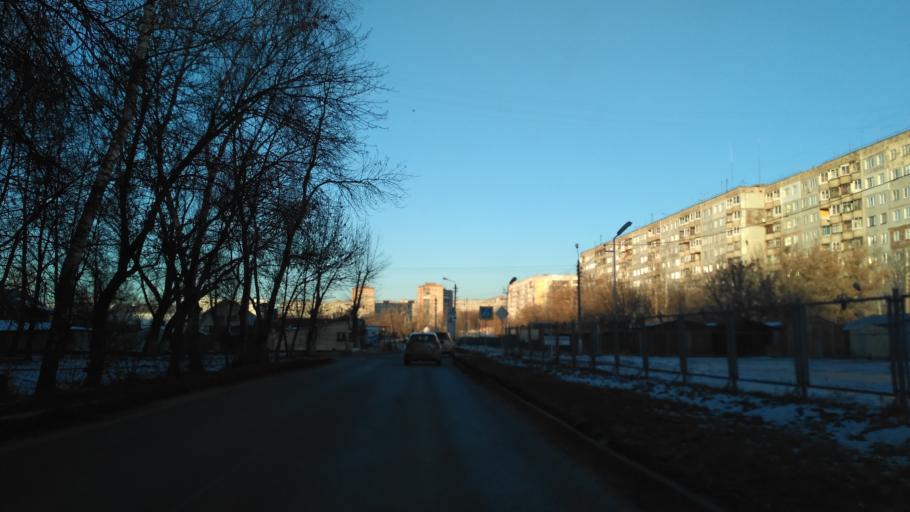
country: RU
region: Tula
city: Tula
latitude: 54.2118
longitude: 37.5967
